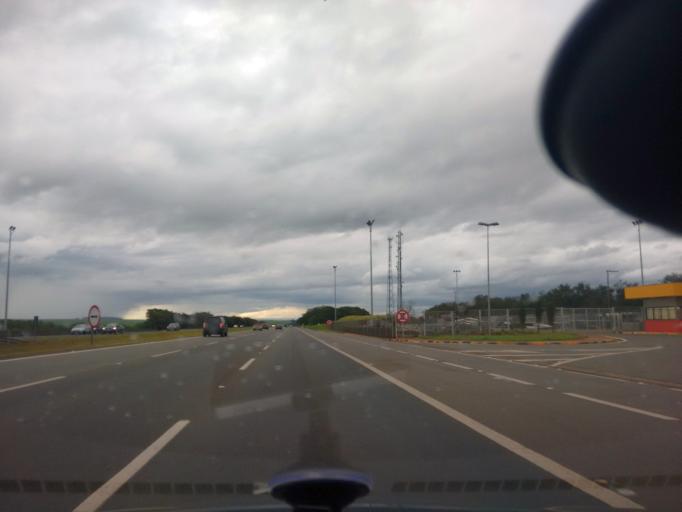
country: BR
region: Sao Paulo
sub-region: Santa Barbara D'Oeste
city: Santa Barbara d'Oeste
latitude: -22.8118
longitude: -47.3884
